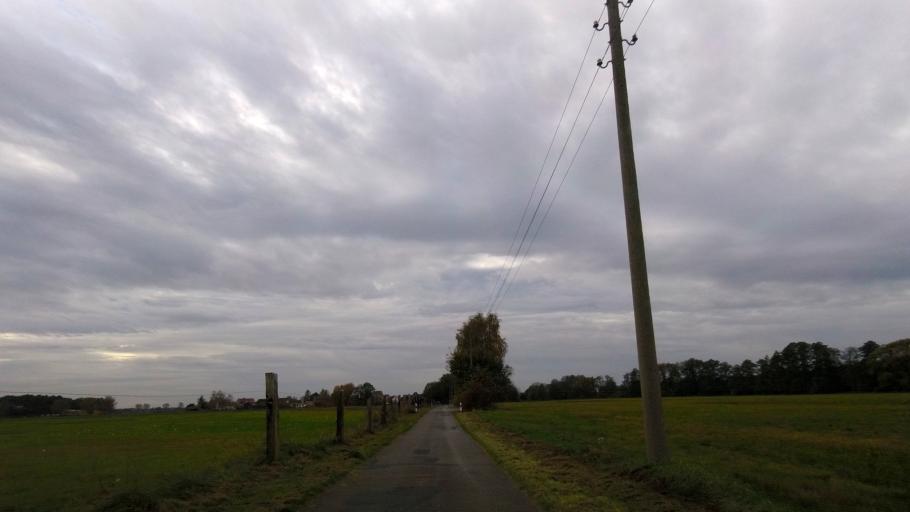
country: DE
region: Brandenburg
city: Borkheide
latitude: 52.1913
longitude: 12.9092
